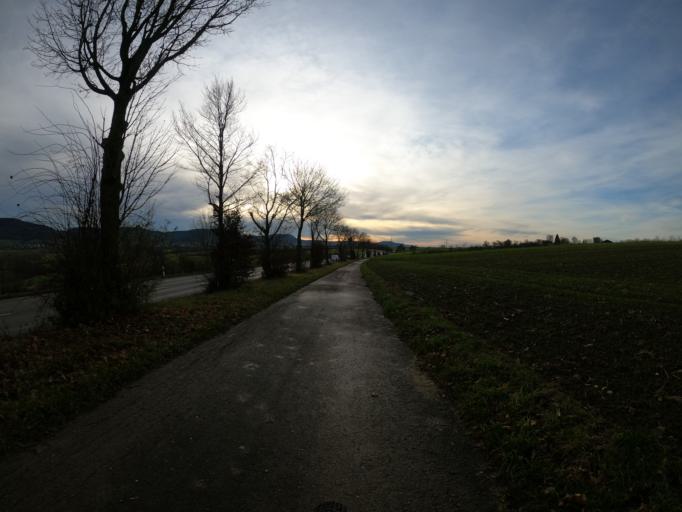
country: DE
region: Baden-Wuerttemberg
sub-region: Regierungsbezirk Stuttgart
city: Heiningen
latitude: 48.6785
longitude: 9.6619
